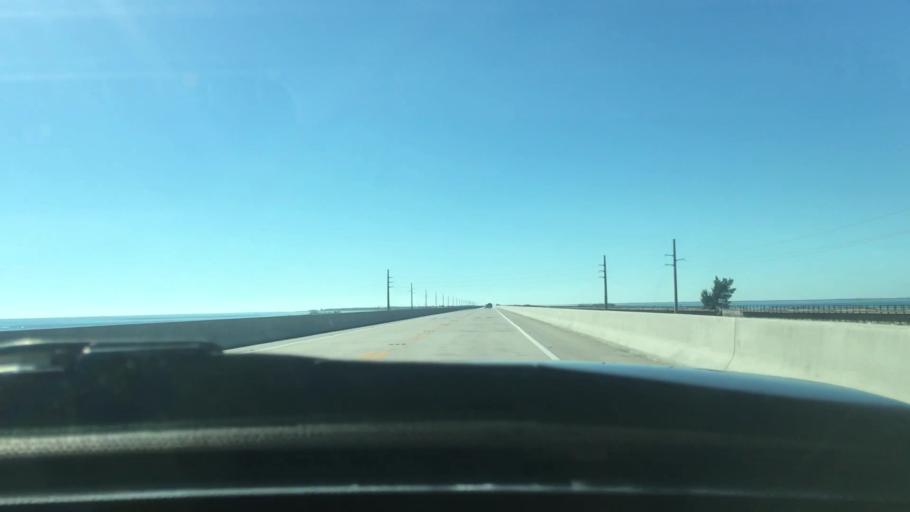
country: US
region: Florida
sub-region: Monroe County
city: Marathon
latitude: 24.6898
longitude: -81.2022
